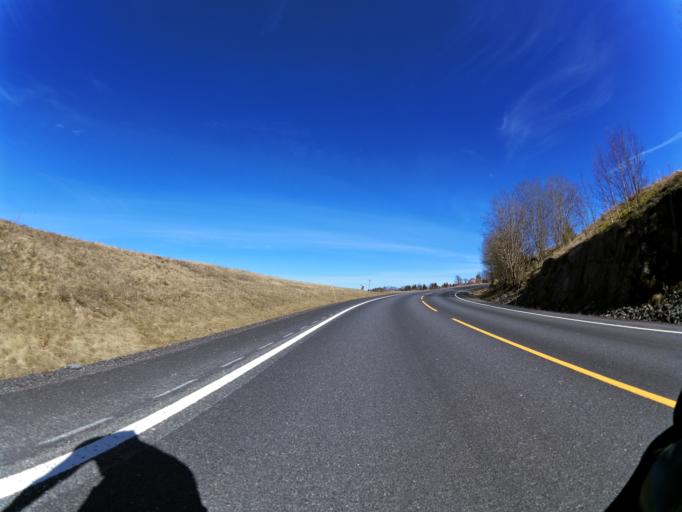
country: NO
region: Ostfold
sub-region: Rade
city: Karlshus
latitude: 59.3258
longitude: 10.9658
